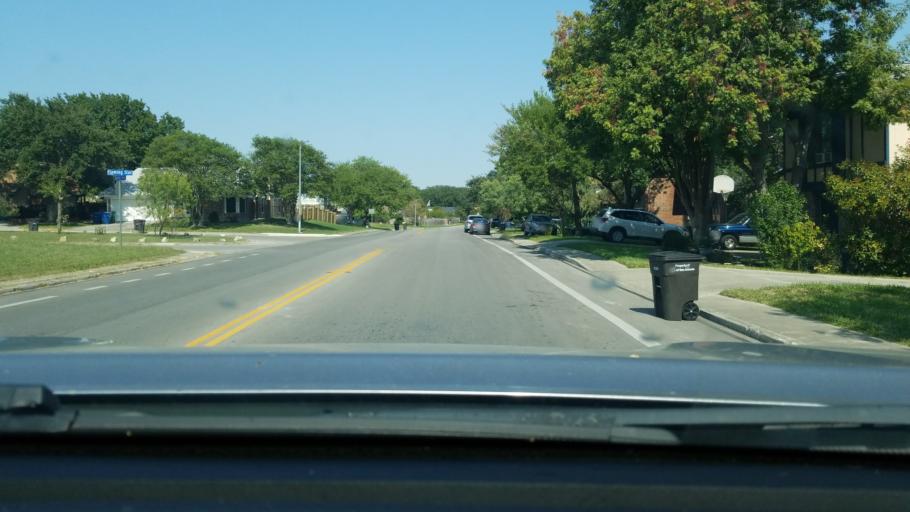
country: US
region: Texas
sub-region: Bexar County
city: Leon Valley
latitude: 29.5528
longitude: -98.6126
